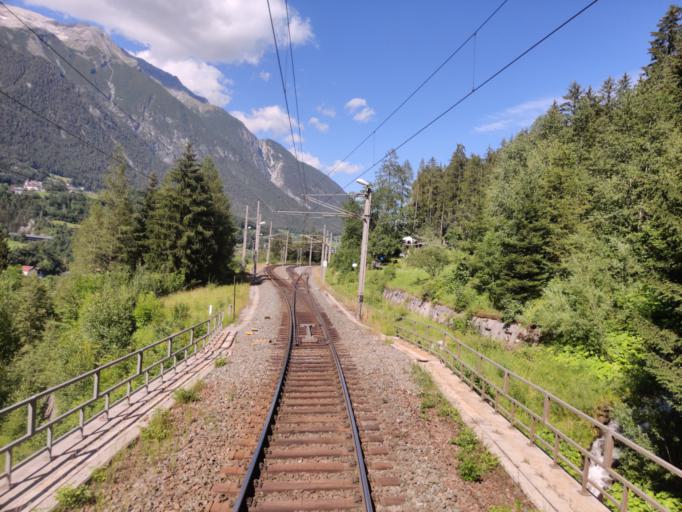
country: AT
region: Tyrol
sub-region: Politischer Bezirk Landeck
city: Pians
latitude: 47.1284
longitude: 10.5067
